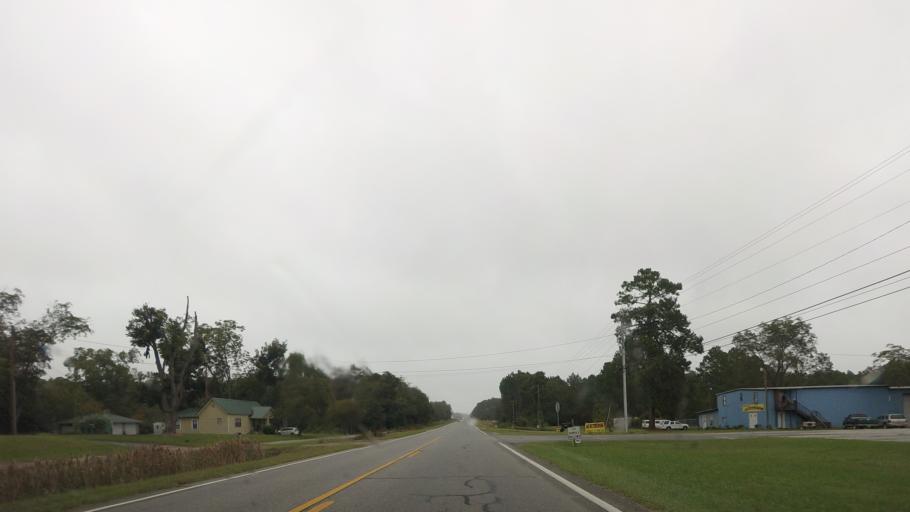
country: US
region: Georgia
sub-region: Ben Hill County
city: Fitzgerald
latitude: 31.7324
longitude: -83.2461
